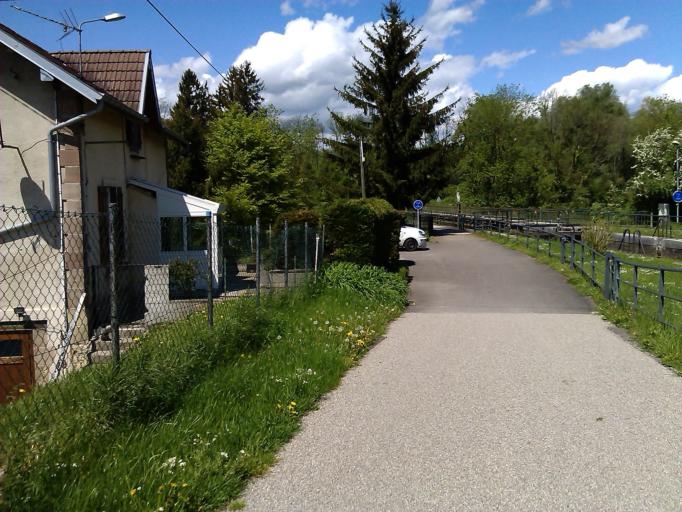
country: FR
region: Franche-Comte
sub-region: Departement du Doubs
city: Etupes
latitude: 47.5224
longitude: 6.8810
